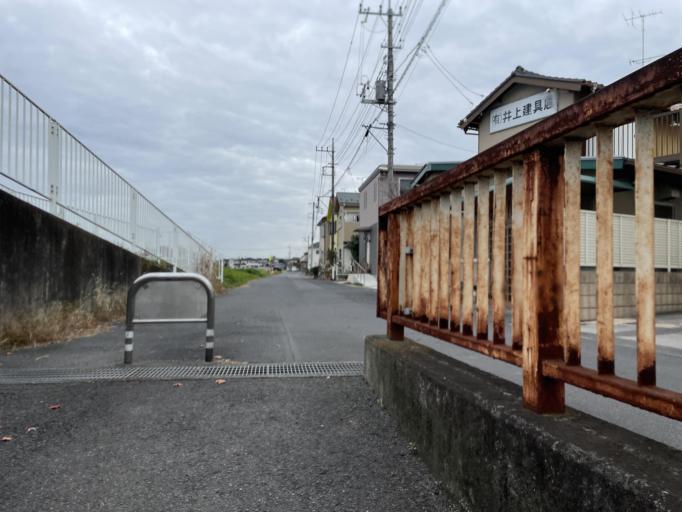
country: JP
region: Saitama
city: Shiraoka
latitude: 36.0295
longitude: 139.6519
